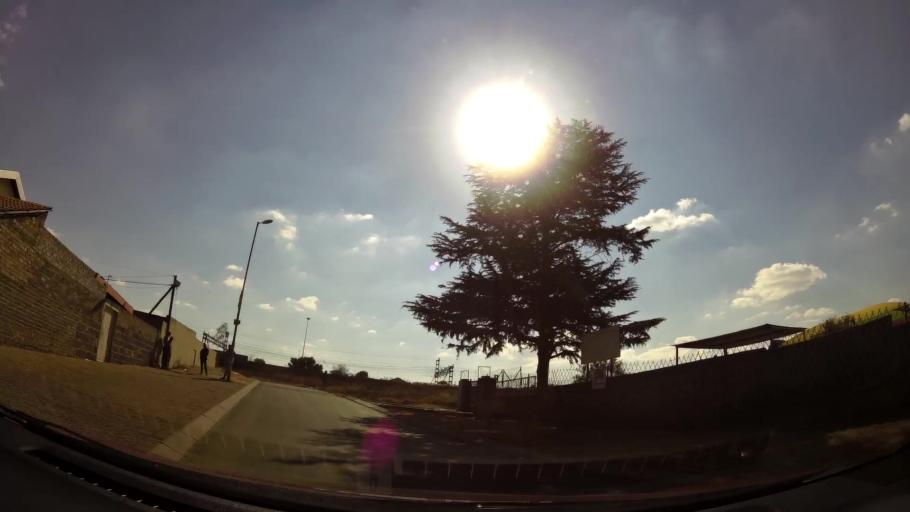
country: ZA
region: Gauteng
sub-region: City of Johannesburg Metropolitan Municipality
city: Soweto
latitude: -26.2263
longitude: 27.9150
